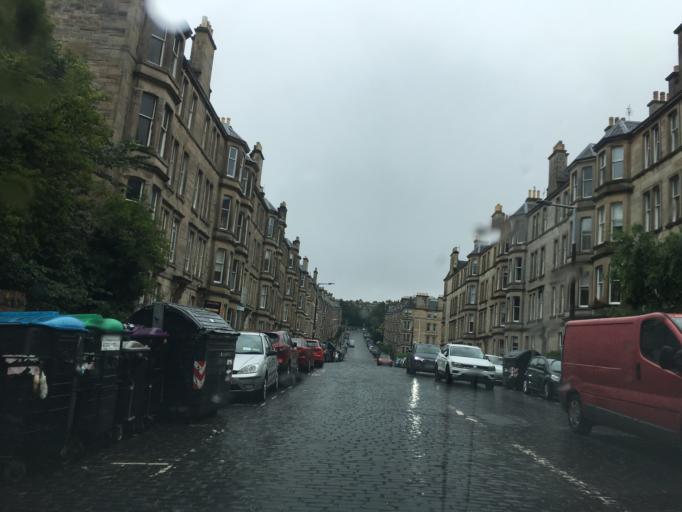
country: GB
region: Scotland
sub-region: Edinburgh
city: Edinburgh
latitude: 55.9594
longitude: -3.2185
